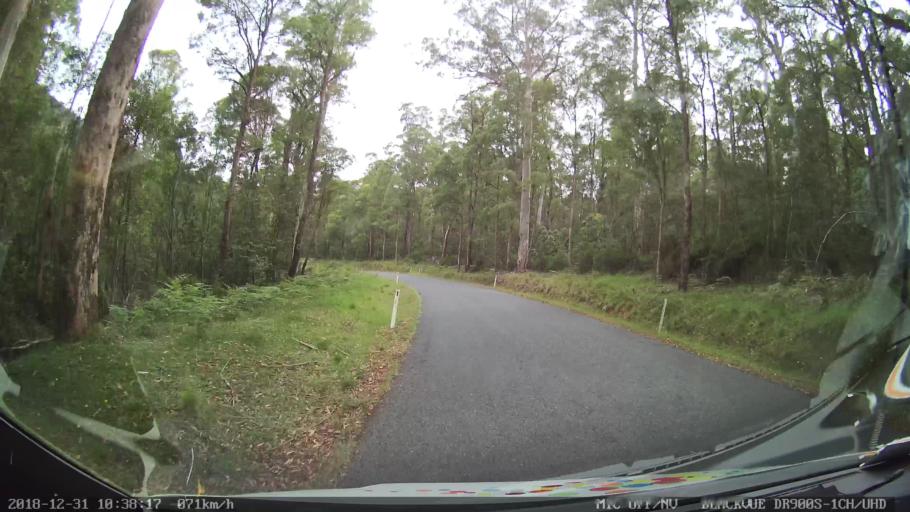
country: AU
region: New South Wales
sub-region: Snowy River
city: Jindabyne
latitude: -36.4089
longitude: 148.1779
